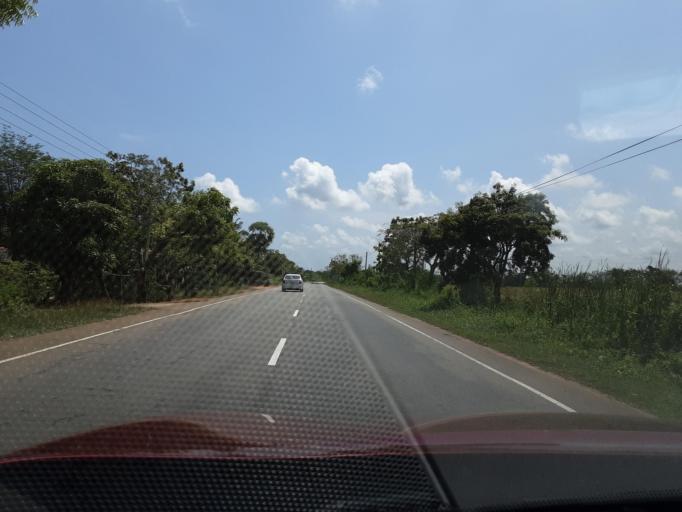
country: LK
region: Southern
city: Tangalla
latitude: 6.2170
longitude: 81.2115
